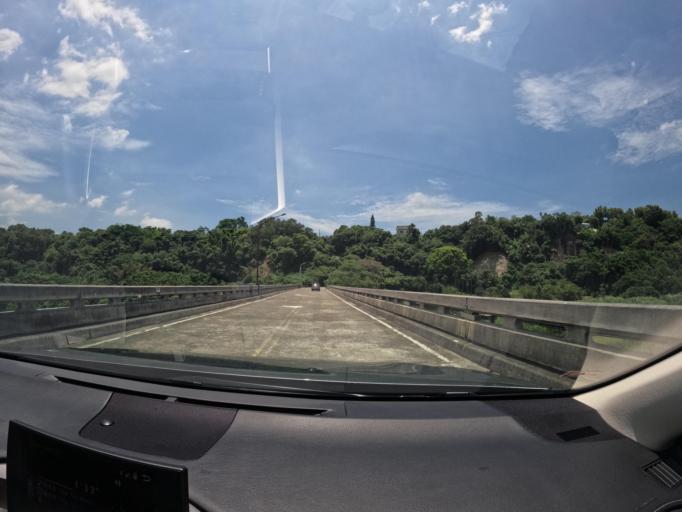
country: TW
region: Taiwan
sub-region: Hsinchu
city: Hsinchu
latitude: 24.6761
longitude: 120.9489
